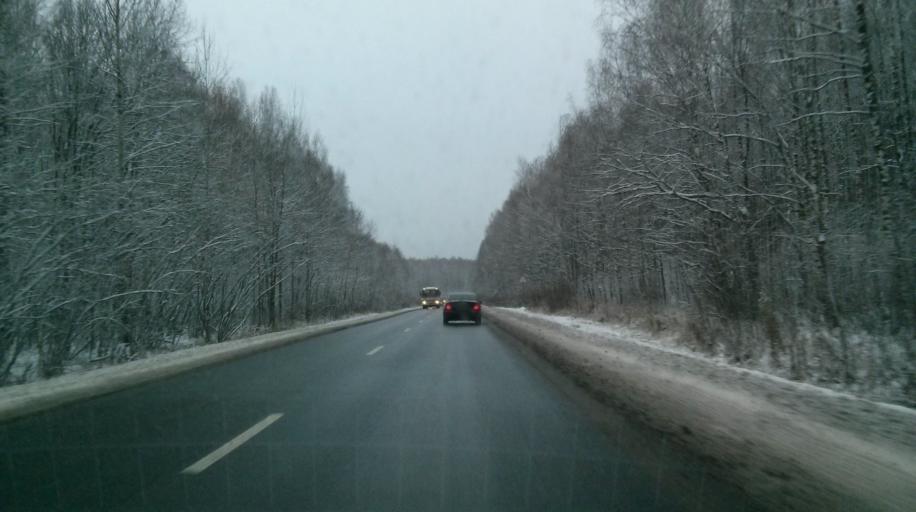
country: RU
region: Nizjnij Novgorod
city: Vorsma
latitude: 56.0167
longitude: 43.3470
